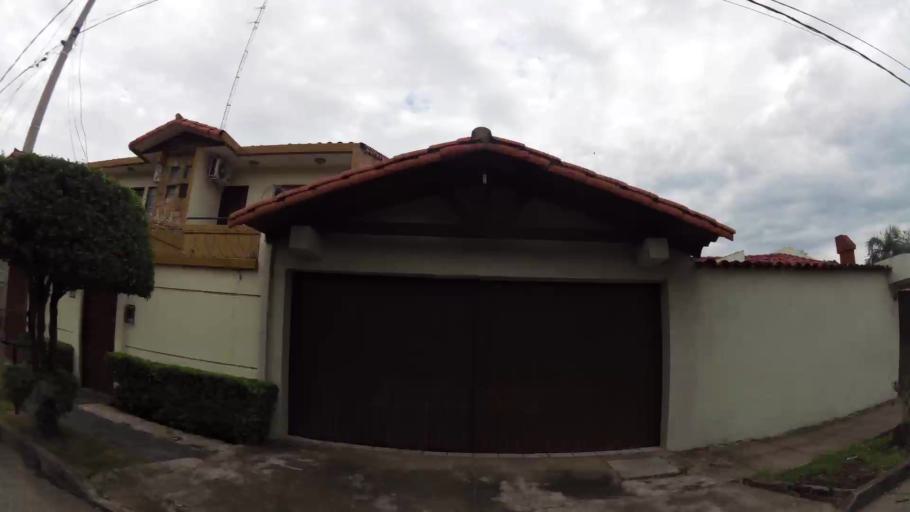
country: BO
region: Santa Cruz
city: Santa Cruz de la Sierra
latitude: -17.7664
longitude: -63.1746
